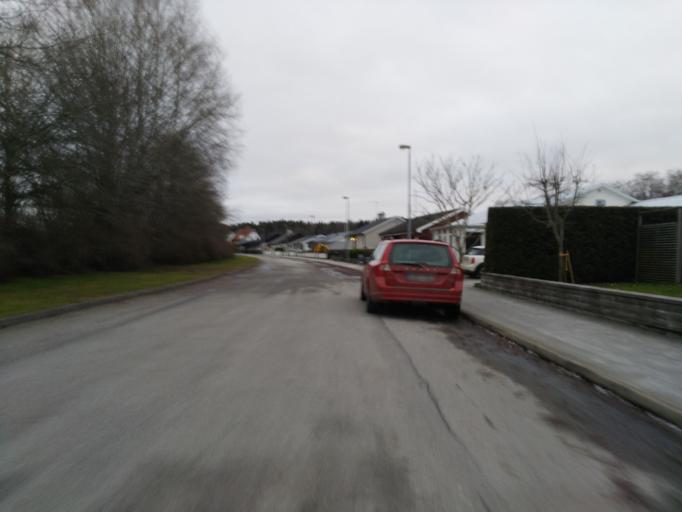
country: SE
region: Vaestra Goetaland
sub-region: Lidkopings Kommun
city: Lidkoping
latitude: 58.4925
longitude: 13.1660
